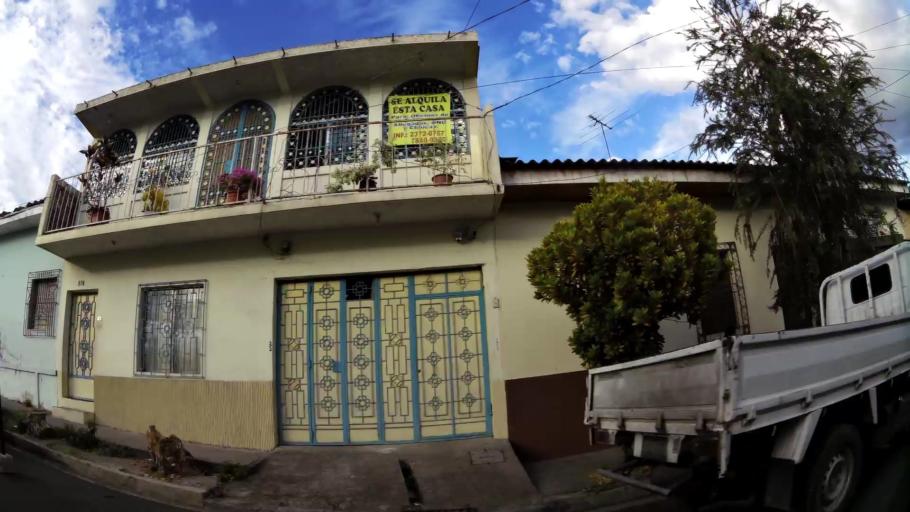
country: SV
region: Cuscatlan
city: Cojutepeque
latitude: 13.7215
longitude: -88.9305
